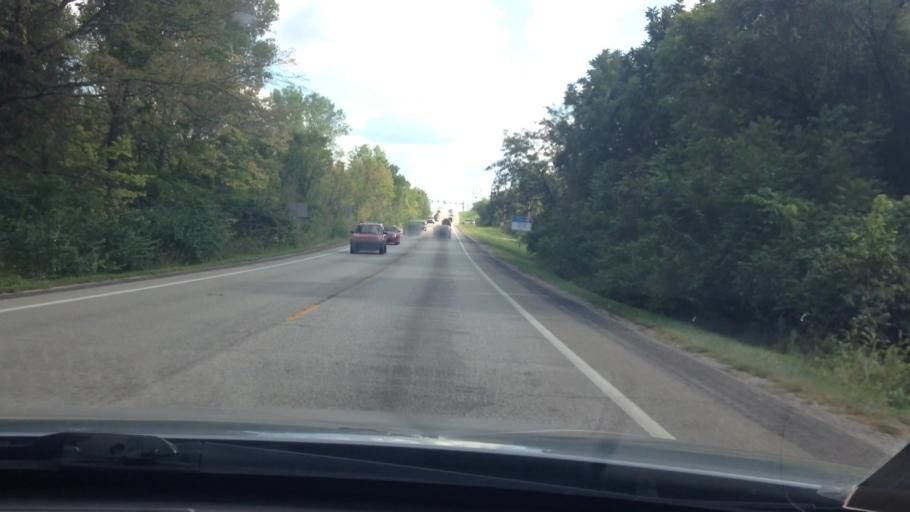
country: US
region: Missouri
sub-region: Clay County
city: Liberty
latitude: 39.2842
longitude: -94.4691
